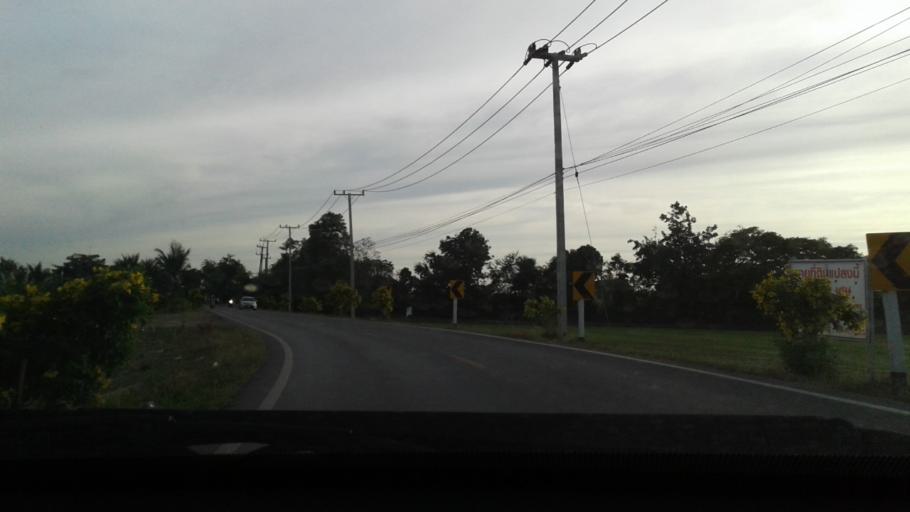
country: TH
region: Nonthaburi
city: Sai Noi
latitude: 13.9211
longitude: 100.2545
